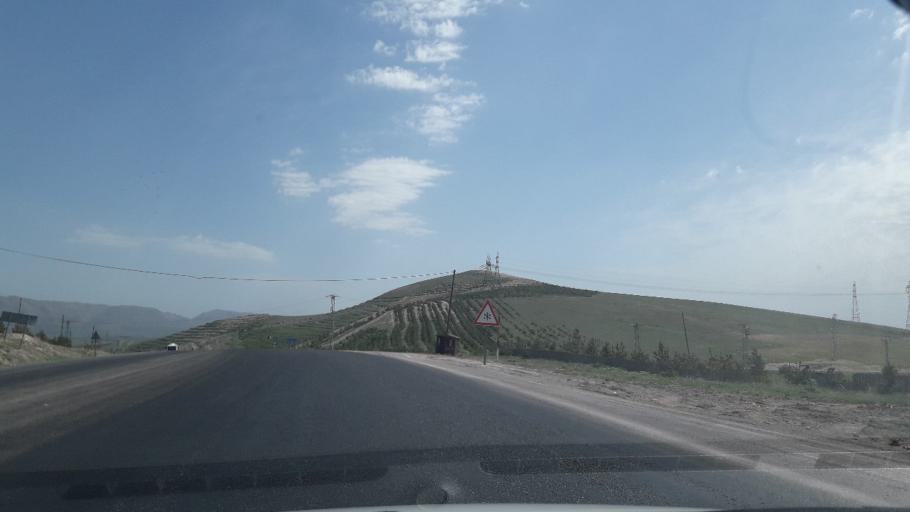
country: TR
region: Sivas
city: Deliktas
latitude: 39.3218
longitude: 37.1421
